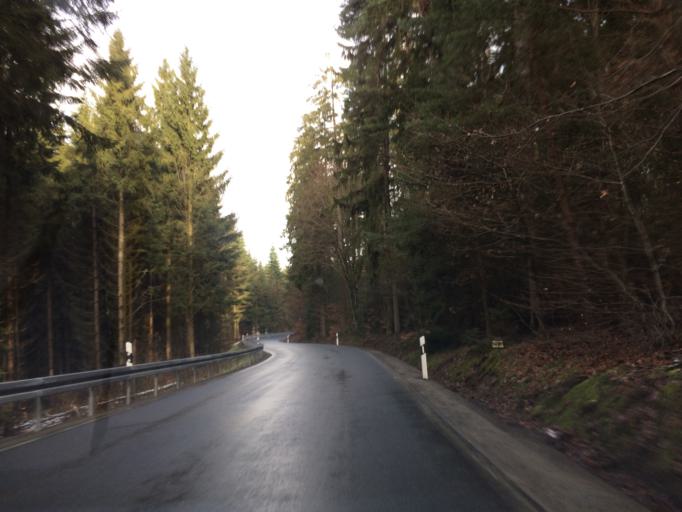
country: DE
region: Hesse
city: Bad Camberg
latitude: 50.3277
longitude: 8.3378
